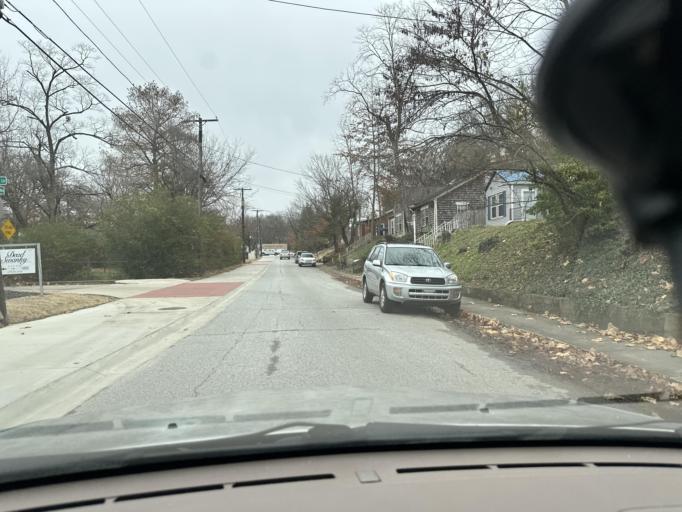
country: US
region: Arkansas
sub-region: Washington County
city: Fayetteville
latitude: 36.0724
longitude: -94.1593
